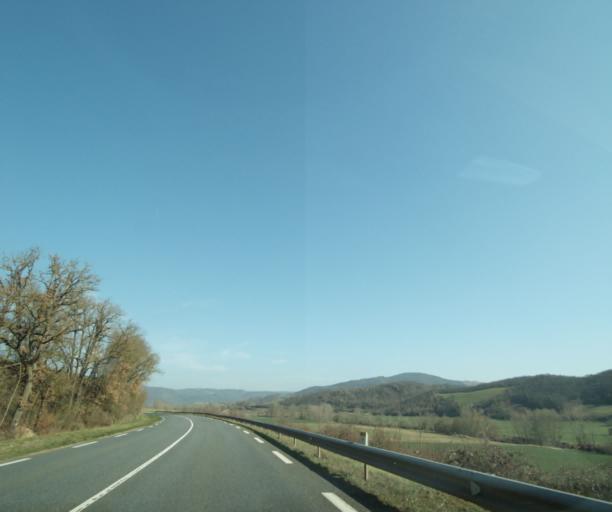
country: FR
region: Midi-Pyrenees
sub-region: Departement de l'Aveyron
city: Saint-Affrique
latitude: 43.9133
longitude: 2.8250
